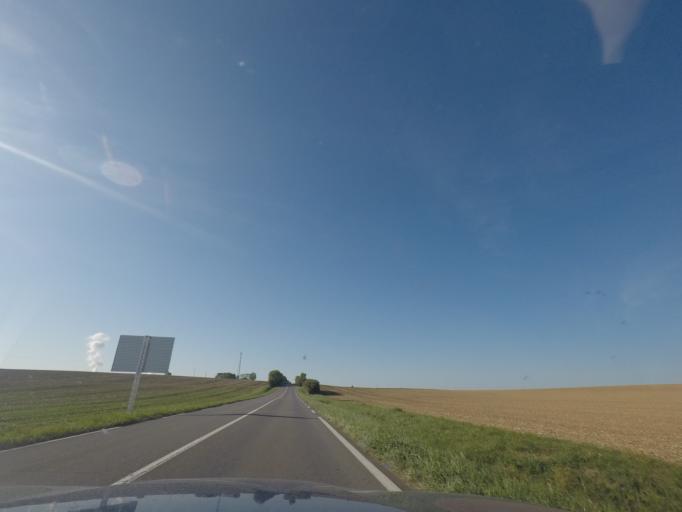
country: LU
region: Luxembourg
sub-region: Canton d'Esch-sur-Alzette
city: Frisange
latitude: 49.4849
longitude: 6.1908
